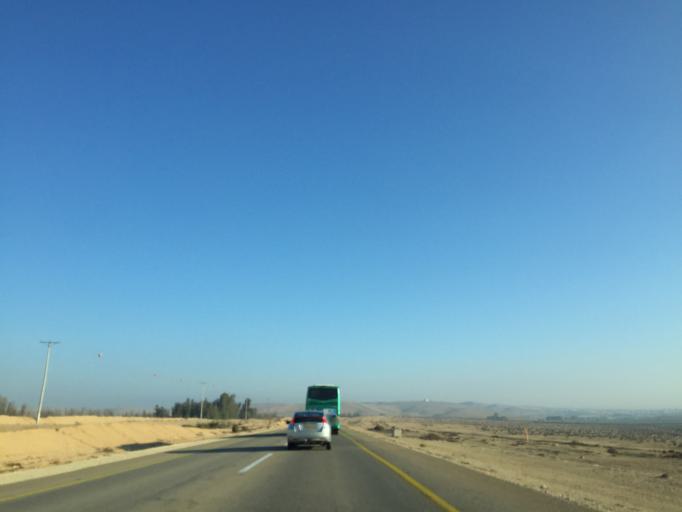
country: IL
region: Southern District
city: Yeroham
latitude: 31.0366
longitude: 34.9754
